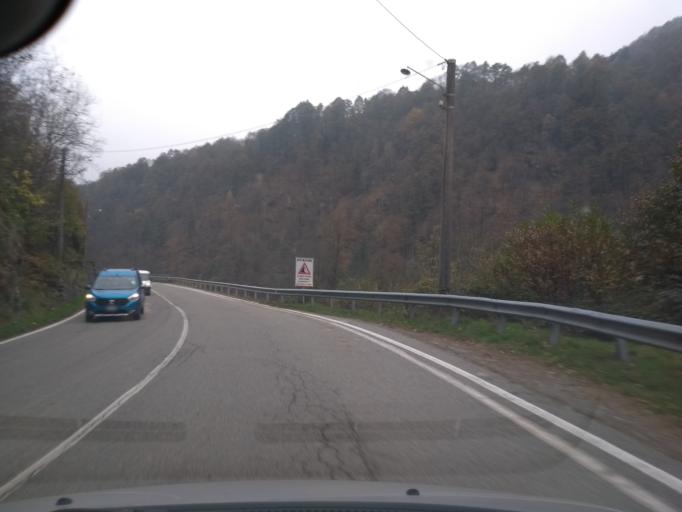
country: IT
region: Piedmont
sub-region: Provincia di Torino
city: Traves
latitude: 45.2747
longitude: 7.4289
